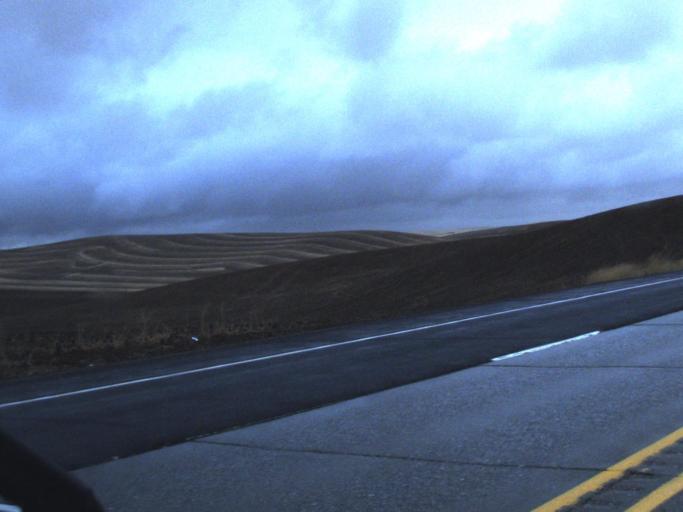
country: US
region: Washington
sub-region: Whitman County
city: Colfax
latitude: 47.1283
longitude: -117.3793
